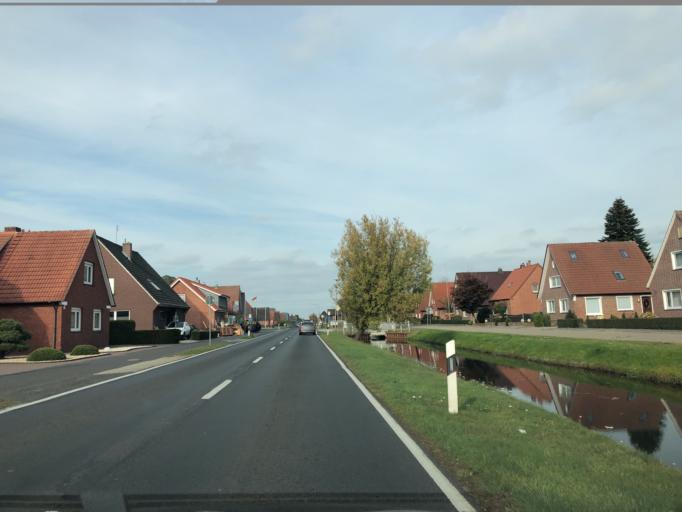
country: DE
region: Lower Saxony
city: Papenburg
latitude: 53.0501
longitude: 7.4598
